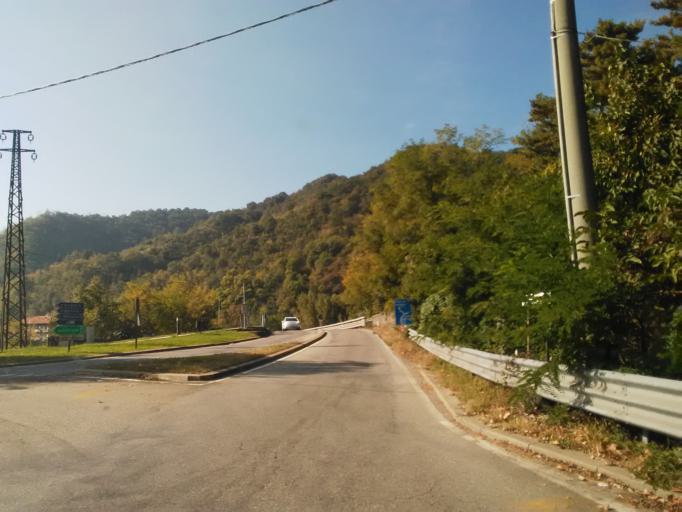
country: IT
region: Piedmont
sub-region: Provincia di Novara
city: Romagnano Sesia
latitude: 45.6374
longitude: 8.3749
